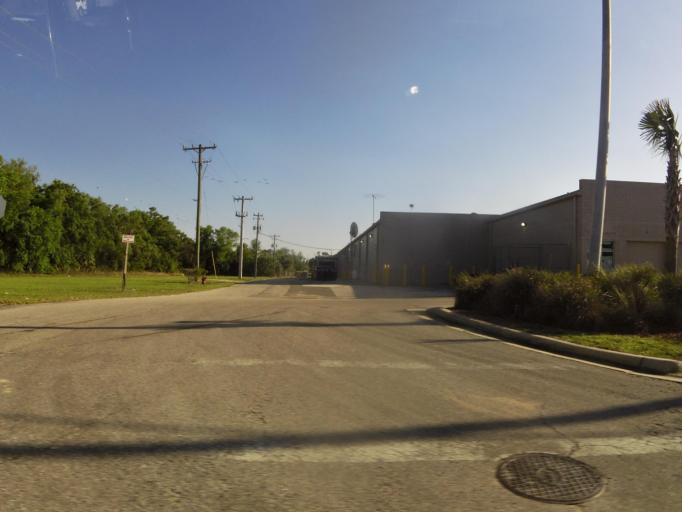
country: US
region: Florida
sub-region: Putnam County
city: Palatka
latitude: 29.6484
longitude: -81.6713
